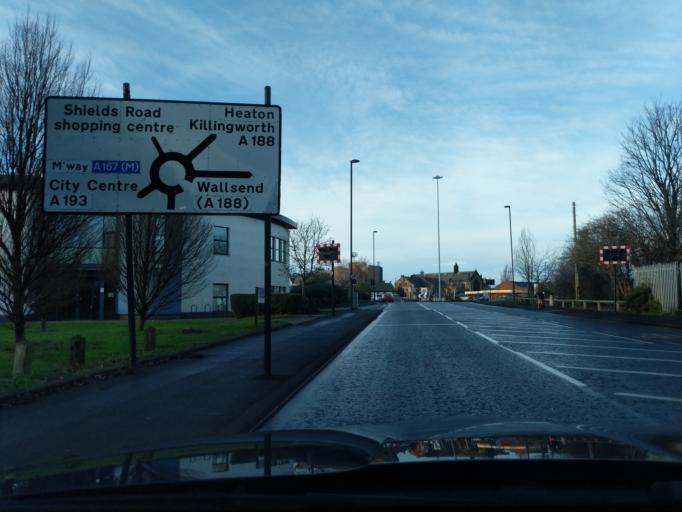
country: GB
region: England
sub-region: Gateshead
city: Felling
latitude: 54.9770
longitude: -1.5727
